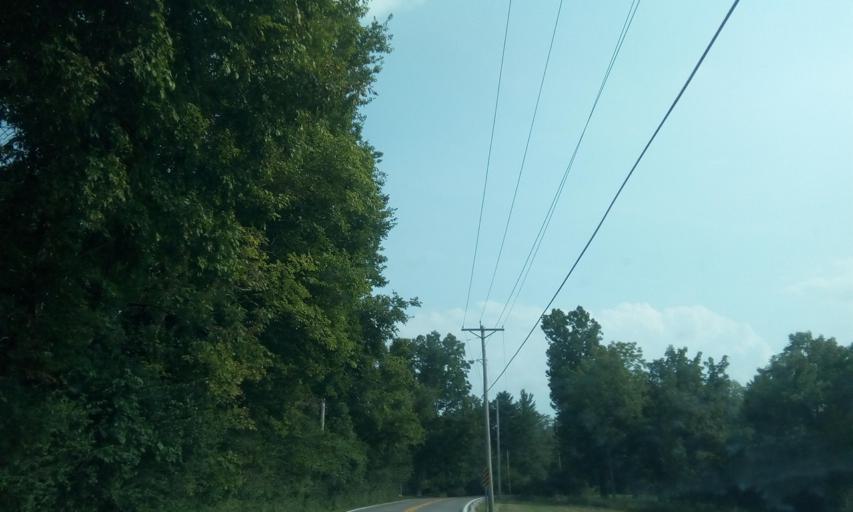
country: US
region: Missouri
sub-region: Saint Louis County
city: Town and Country
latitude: 38.6028
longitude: -90.4819
